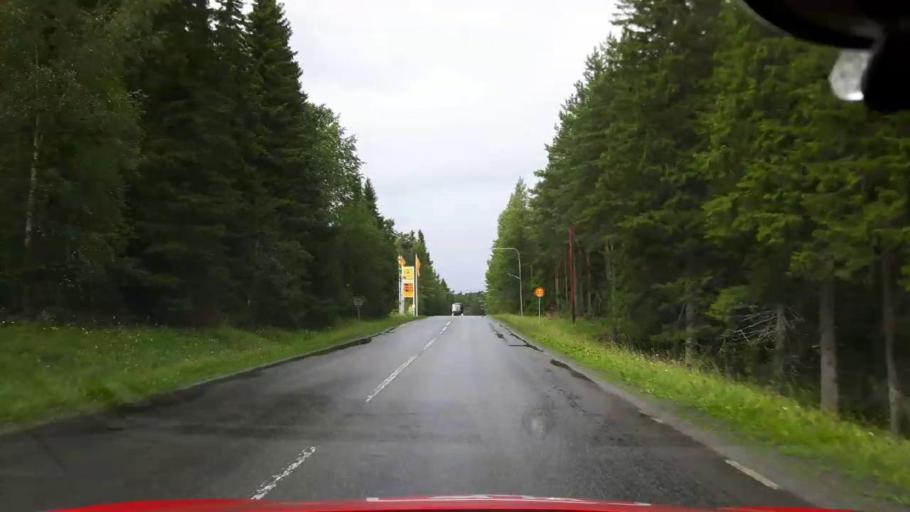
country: SE
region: Jaemtland
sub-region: Krokoms Kommun
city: Krokom
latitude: 63.3423
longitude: 14.2674
